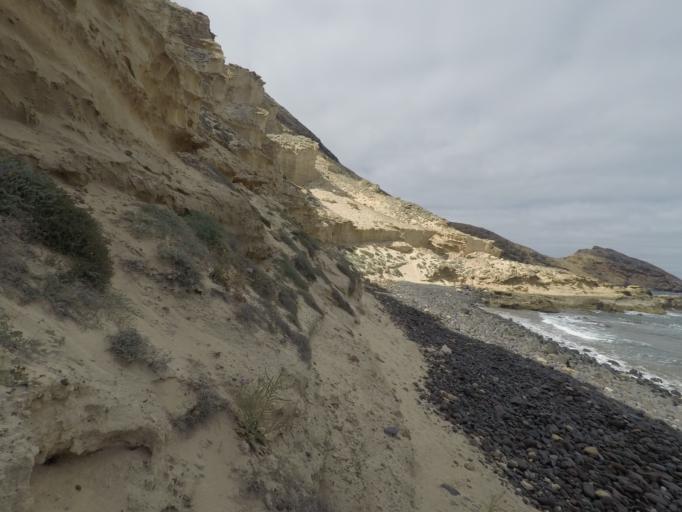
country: PT
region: Madeira
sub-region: Porto Santo
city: Vila de Porto Santo
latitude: 33.0732
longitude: -16.2960
